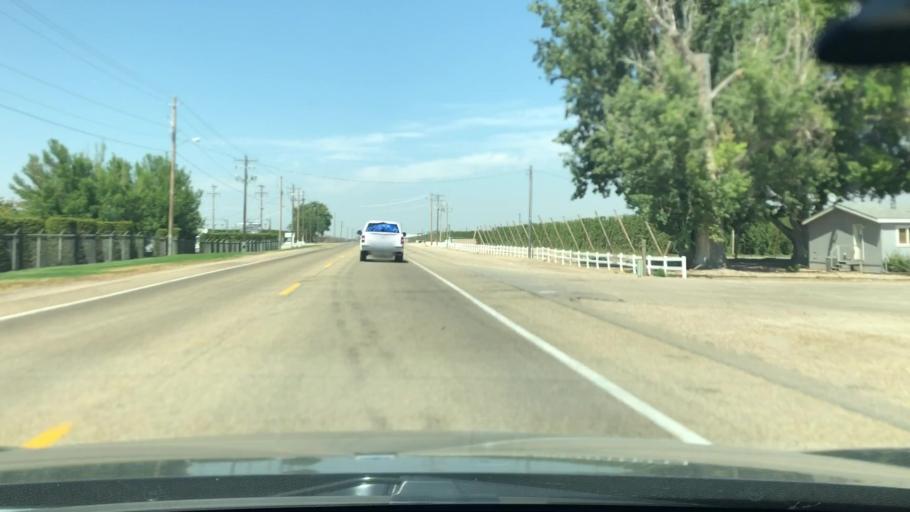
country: US
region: Idaho
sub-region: Canyon County
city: Wilder
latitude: 43.6957
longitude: -116.9120
